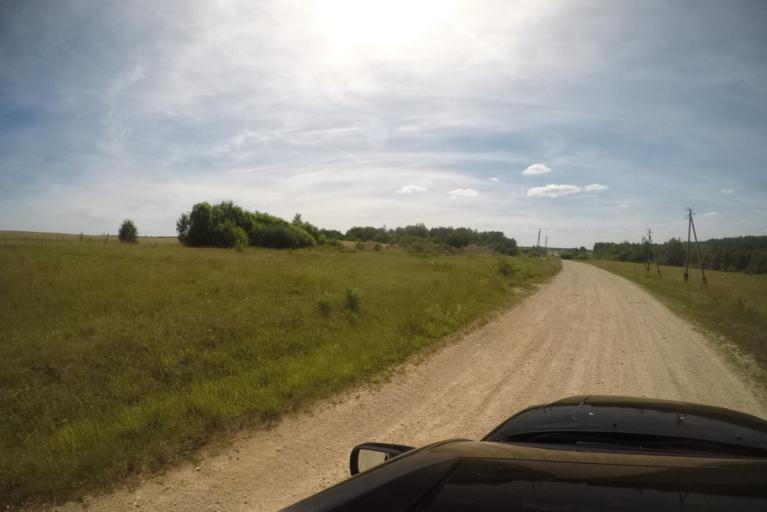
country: BY
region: Grodnenskaya
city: Hal'shany
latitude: 54.2603
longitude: 25.9738
